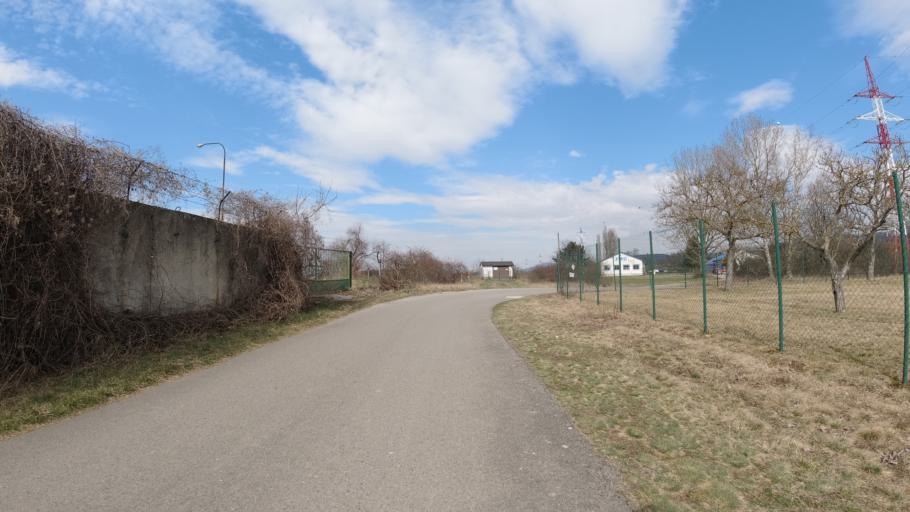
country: SK
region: Trnavsky
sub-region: Okres Trnava
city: Piestany
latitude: 48.6613
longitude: 17.8522
